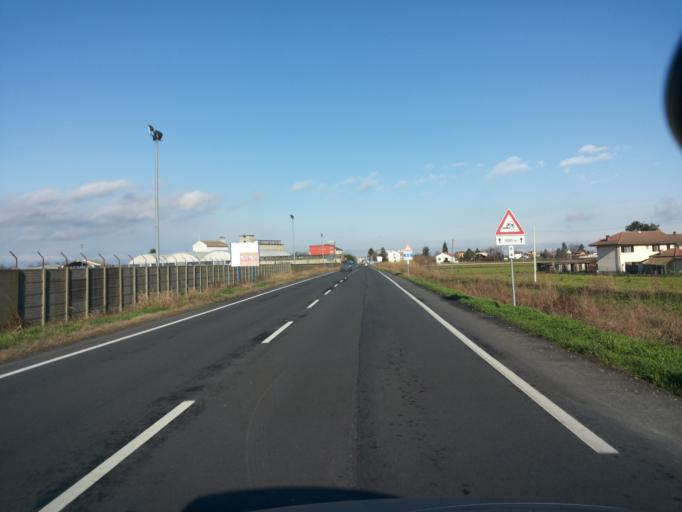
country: IT
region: Piedmont
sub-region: Provincia di Vercelli
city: Borgo Vercelli
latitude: 45.3321
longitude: 8.4489
